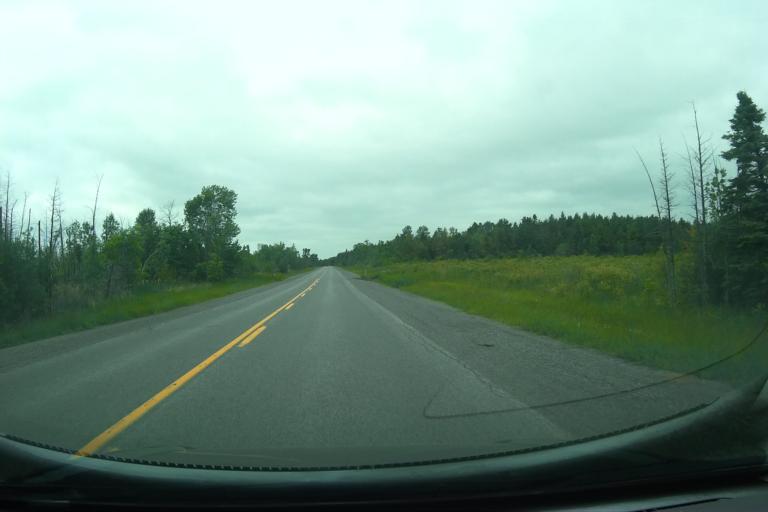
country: CA
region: Ontario
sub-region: Lanark County
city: Smiths Falls
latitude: 45.0118
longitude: -75.8354
